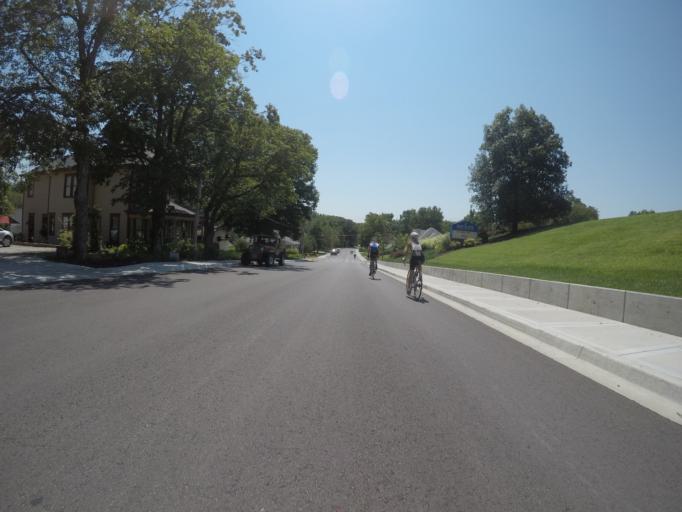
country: US
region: Missouri
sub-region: Platte County
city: Weston
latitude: 39.4181
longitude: -94.9008
